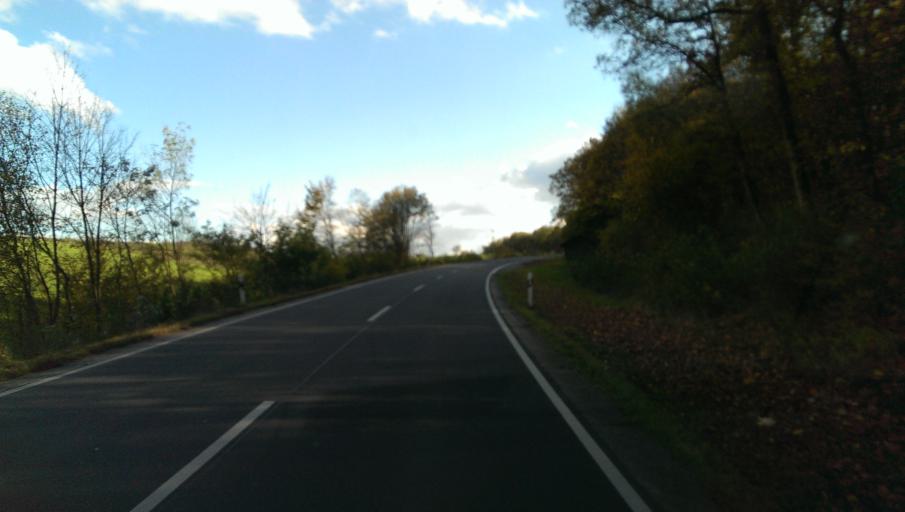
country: DE
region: Baden-Wuerttemberg
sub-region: Karlsruhe Region
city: Billigheim
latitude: 49.4098
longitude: 9.2450
